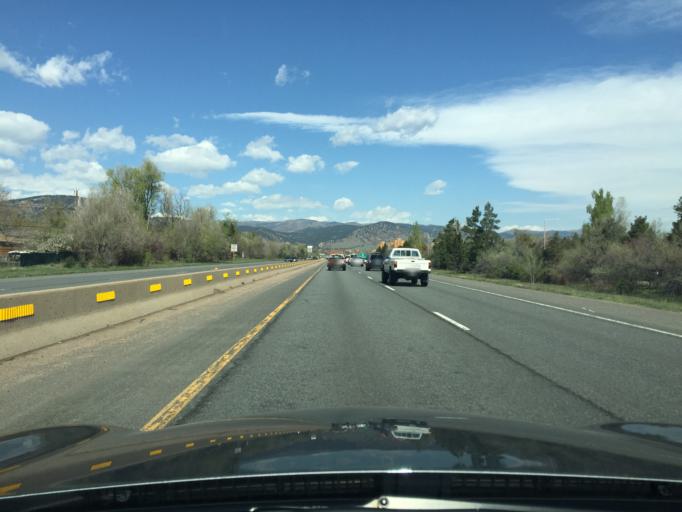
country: US
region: Colorado
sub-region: Boulder County
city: Boulder
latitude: 39.9902
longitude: -105.2413
